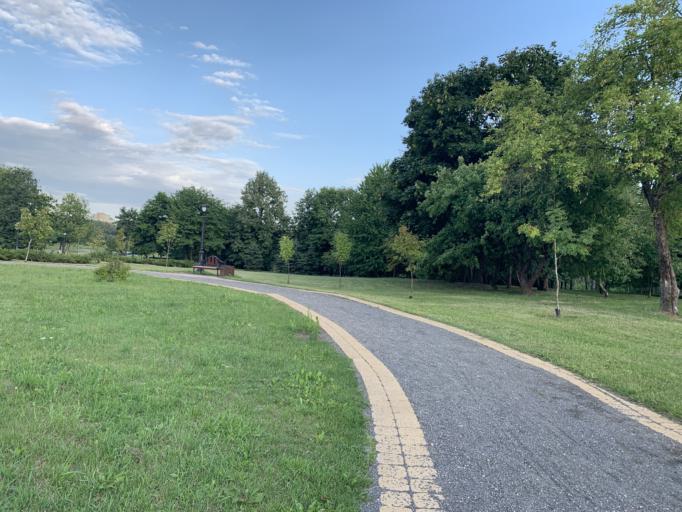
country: BY
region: Minsk
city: Minsk
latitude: 53.8537
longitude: 27.5824
